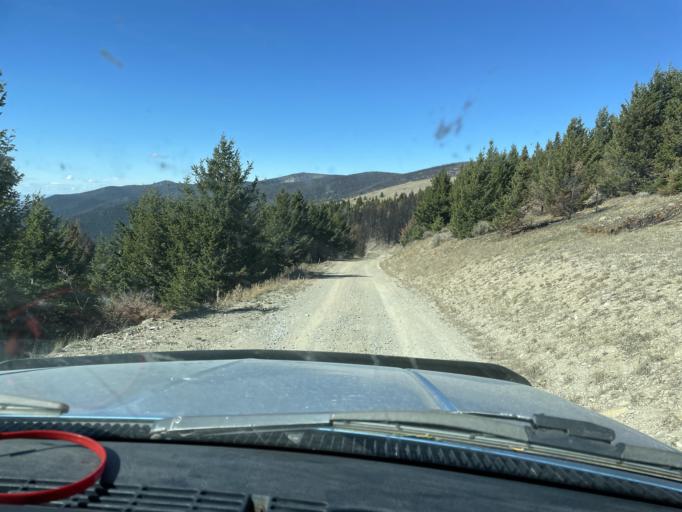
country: US
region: Montana
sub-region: Broadwater County
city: Townsend
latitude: 46.5000
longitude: -111.2705
